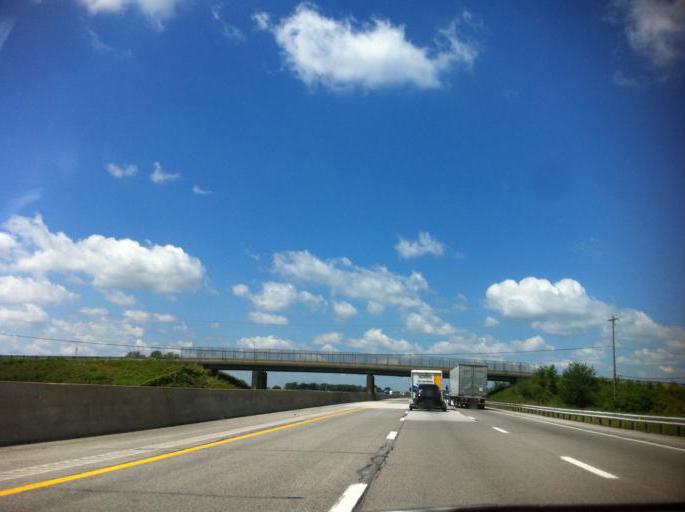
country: US
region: Ohio
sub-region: Sandusky County
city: Stony Prairie
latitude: 41.4296
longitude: -83.1996
